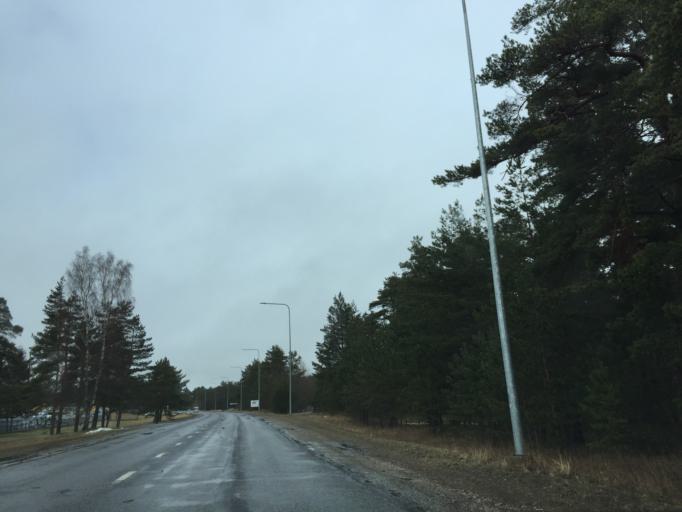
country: EE
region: Laeaene
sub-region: Haapsalu linn
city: Haapsalu
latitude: 58.9193
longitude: 23.5492
